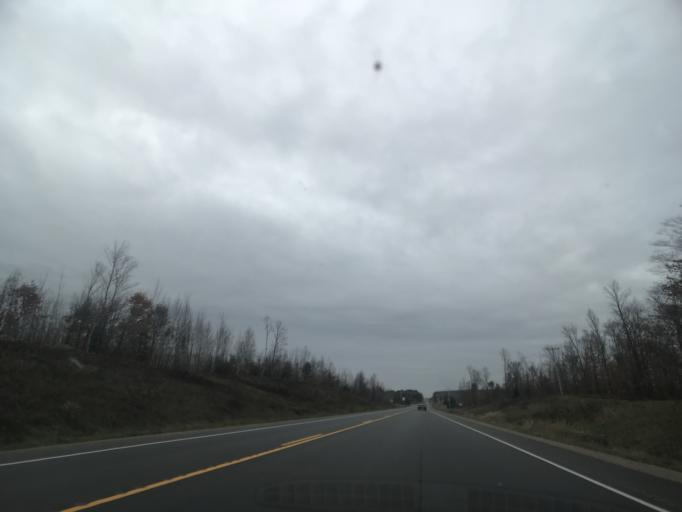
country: US
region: Wisconsin
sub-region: Menominee County
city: Legend Lake
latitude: 45.2333
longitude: -88.5162
